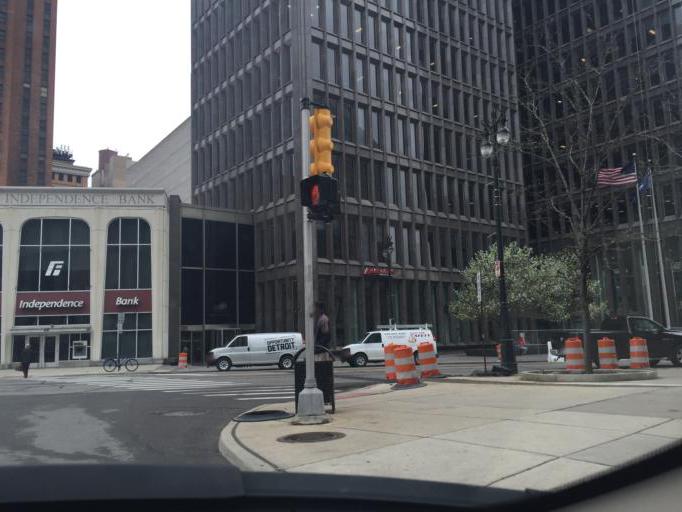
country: US
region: Michigan
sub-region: Wayne County
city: Detroit
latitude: 42.3314
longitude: -83.0480
